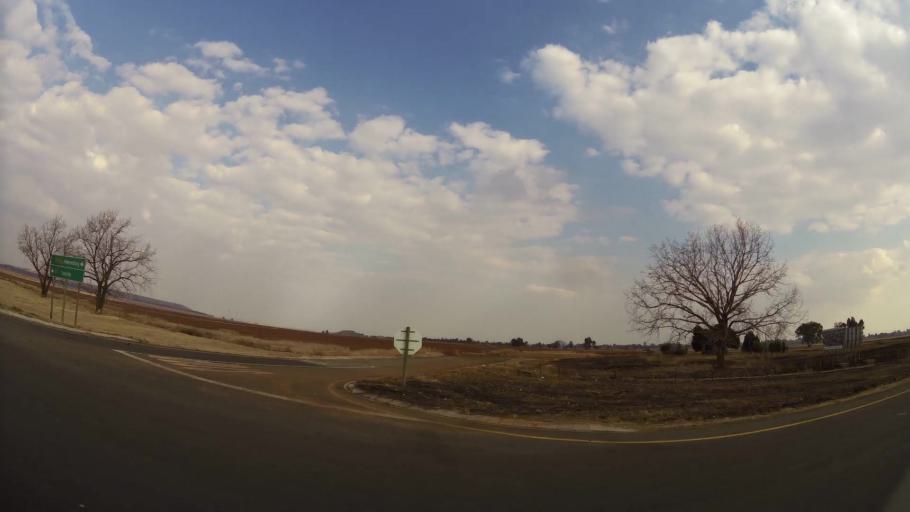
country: ZA
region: Gauteng
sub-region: Ekurhuleni Metropolitan Municipality
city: Springs
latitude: -26.2691
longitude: 28.4905
